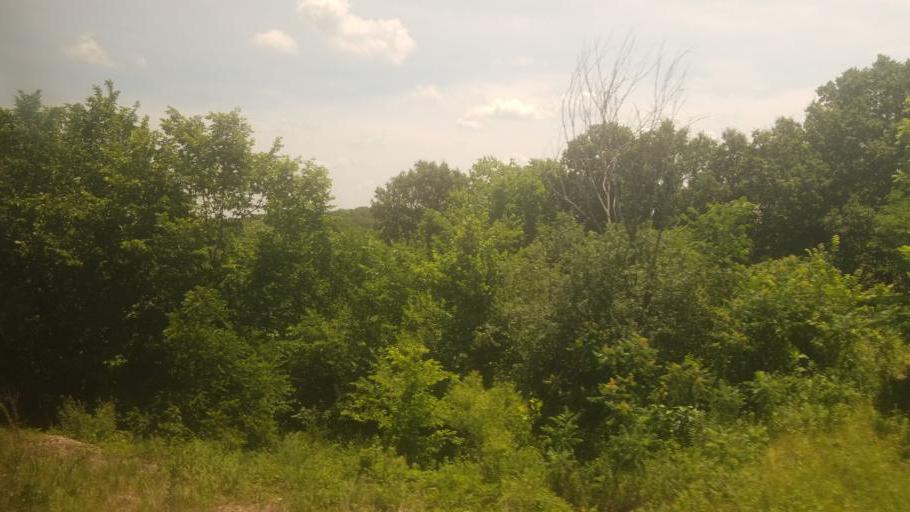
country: US
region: Missouri
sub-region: Linn County
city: Marceline
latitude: 39.8637
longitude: -92.8002
